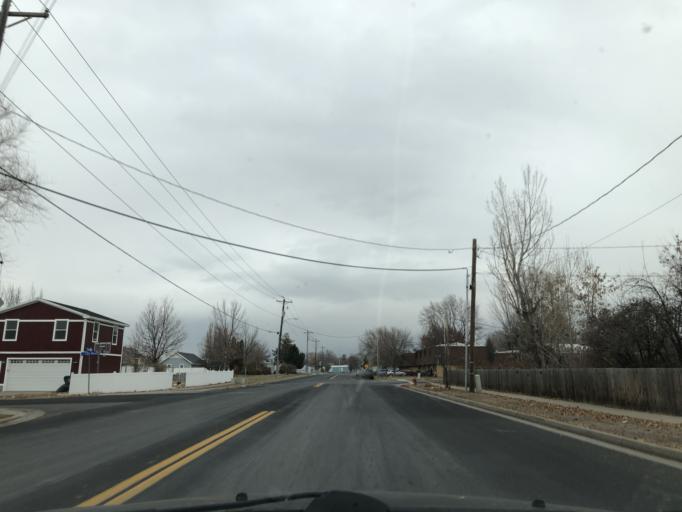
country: US
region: Utah
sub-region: Cache County
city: Logan
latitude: 41.7238
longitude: -111.8530
